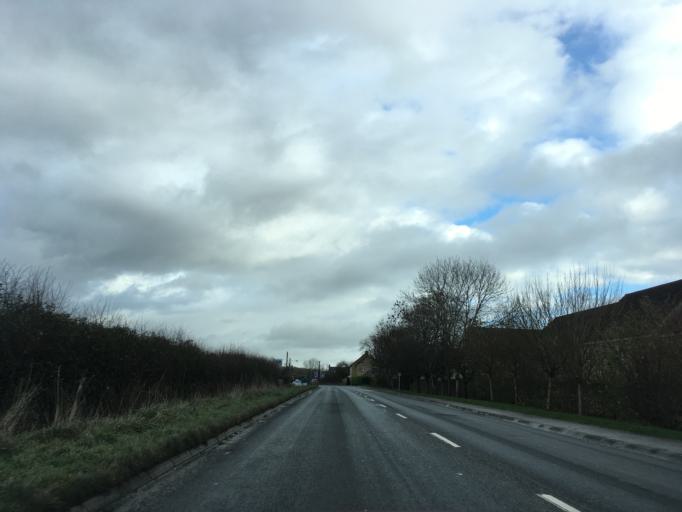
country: GB
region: England
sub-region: Wiltshire
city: Malmesbury
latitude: 51.5970
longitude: -2.1016
